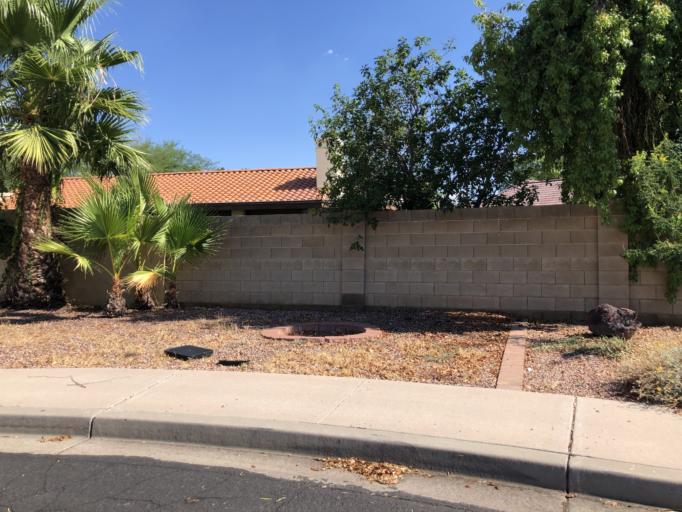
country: US
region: Arizona
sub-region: Maricopa County
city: Gilbert
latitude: 33.4010
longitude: -111.7722
